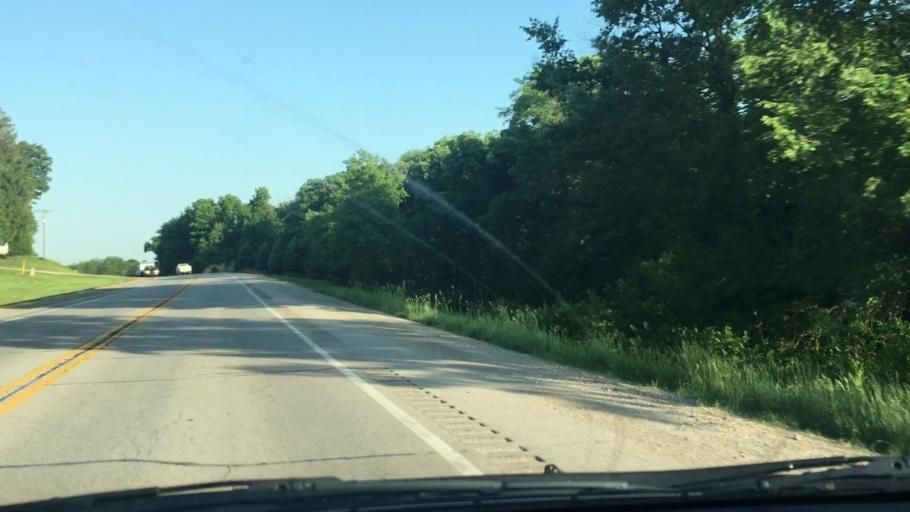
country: US
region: Iowa
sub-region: Johnson County
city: Tiffin
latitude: 41.7107
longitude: -91.6913
